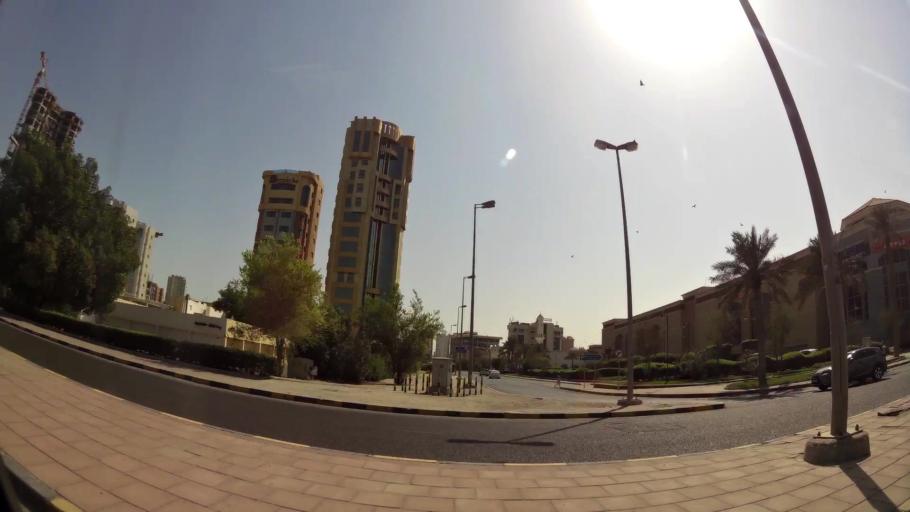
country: KW
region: Muhafazat Hawalli
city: As Salimiyah
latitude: 29.3412
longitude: 48.0667
